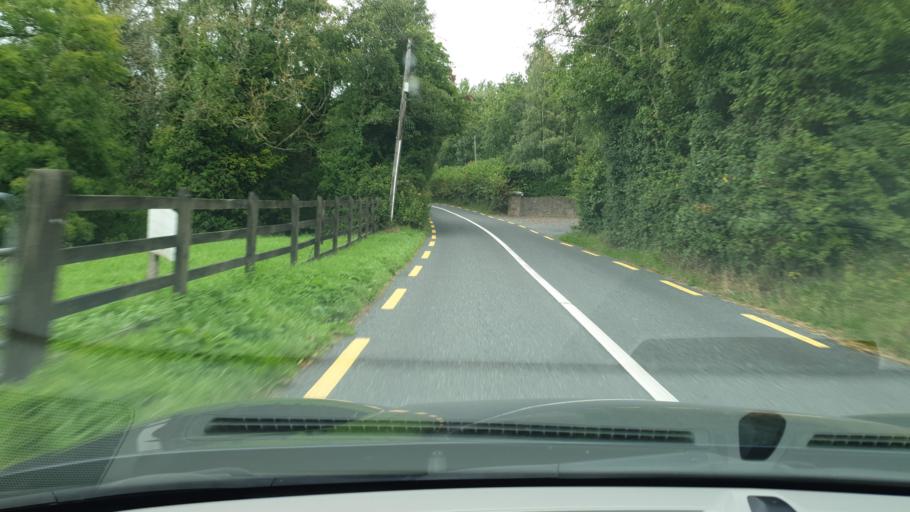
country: IE
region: Leinster
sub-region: Kildare
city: Naas
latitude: 53.2293
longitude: -6.6992
